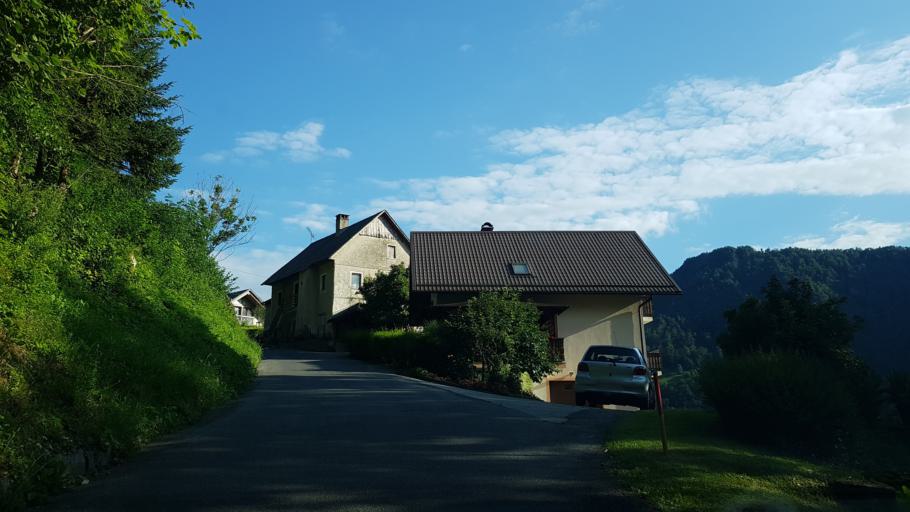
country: SI
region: Cerkno
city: Cerkno
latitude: 46.0877
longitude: 13.9739
